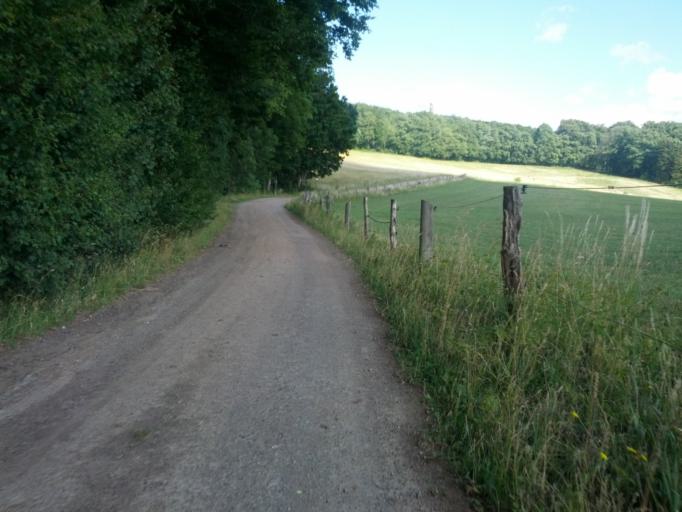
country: DE
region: Thuringia
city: Wolfsburg-Unkeroda
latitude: 50.9669
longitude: 10.2381
